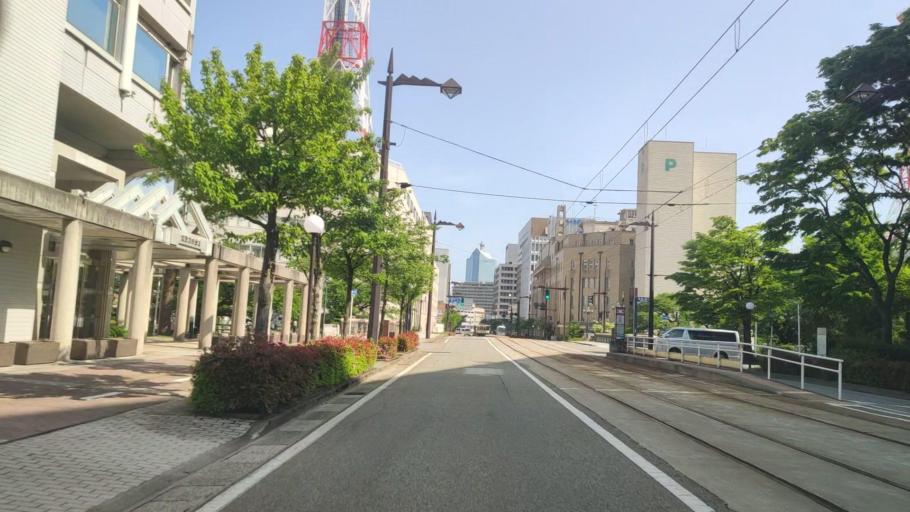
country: JP
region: Toyama
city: Toyama-shi
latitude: 36.6950
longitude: 137.2160
